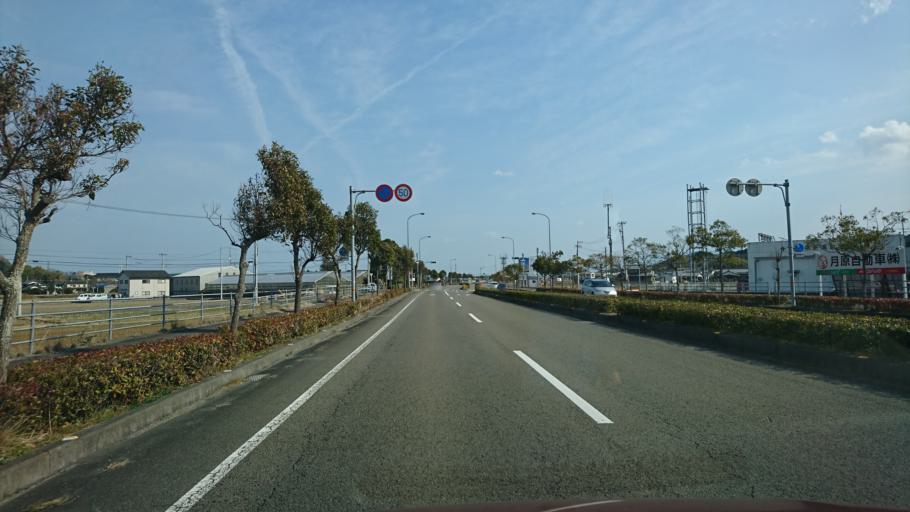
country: JP
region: Ehime
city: Saijo
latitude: 34.0194
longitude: 133.0245
